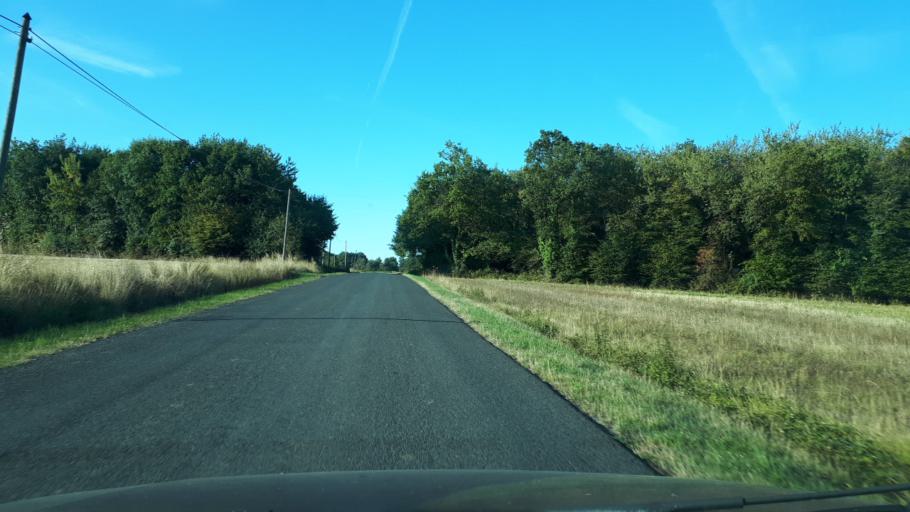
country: FR
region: Centre
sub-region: Departement du Loir-et-Cher
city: Lunay
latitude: 47.7436
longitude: 0.9371
